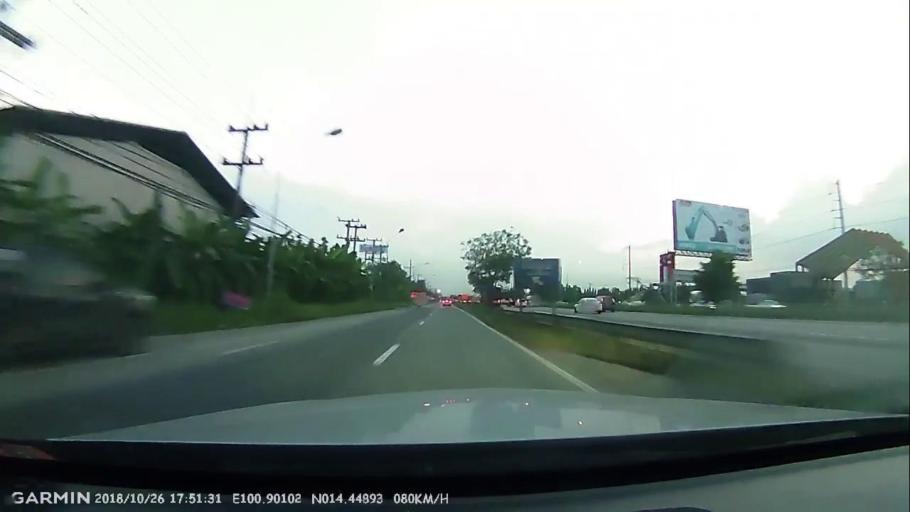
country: TH
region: Sara Buri
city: Saraburi
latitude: 14.4488
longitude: 100.9016
